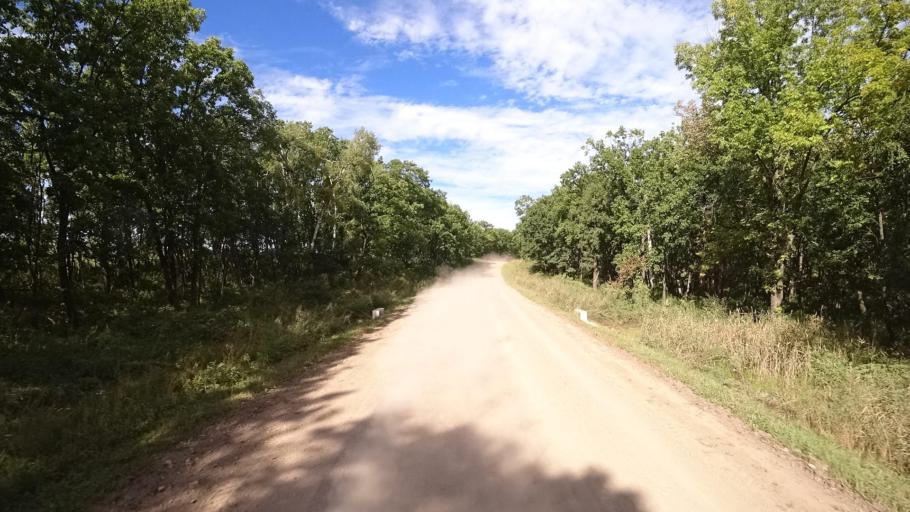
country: RU
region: Primorskiy
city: Yakovlevka
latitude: 44.4054
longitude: 133.5662
